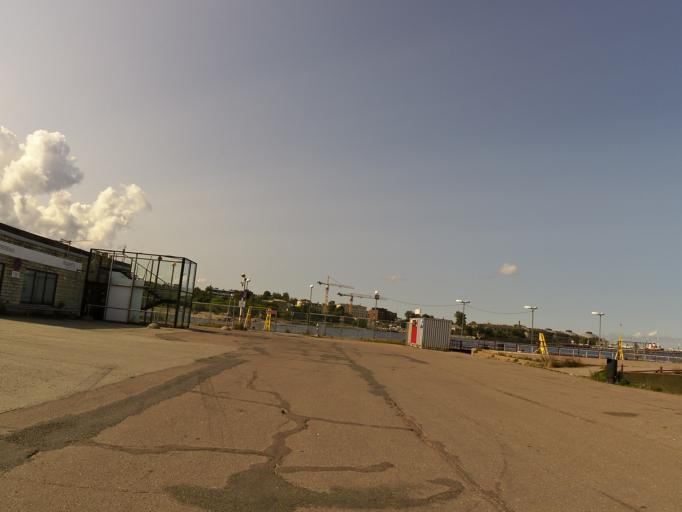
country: EE
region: Harju
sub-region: Tallinna linn
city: Tallinn
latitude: 59.4484
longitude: 24.7534
